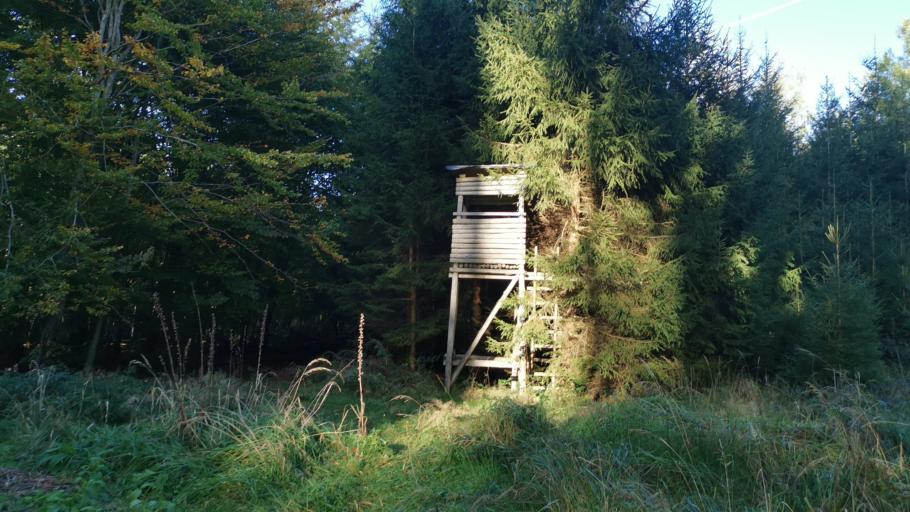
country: DE
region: Bavaria
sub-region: Upper Bavaria
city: Baierbrunn
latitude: 48.0453
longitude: 11.4847
